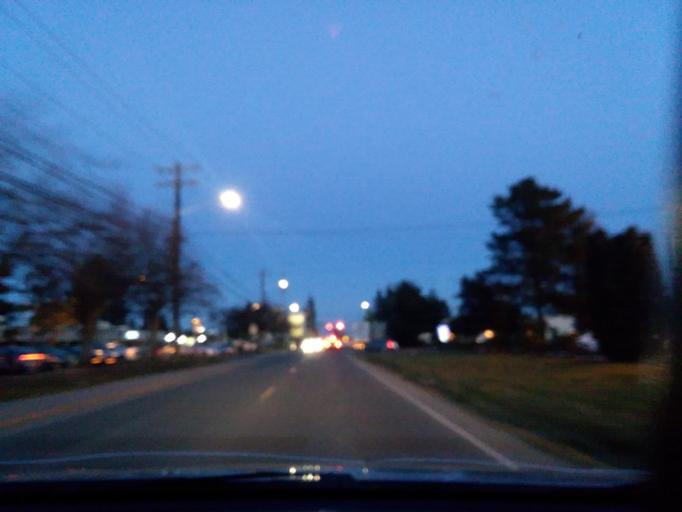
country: US
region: Washington
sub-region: Snohomish County
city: Martha Lake
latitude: 47.9074
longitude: -122.2440
